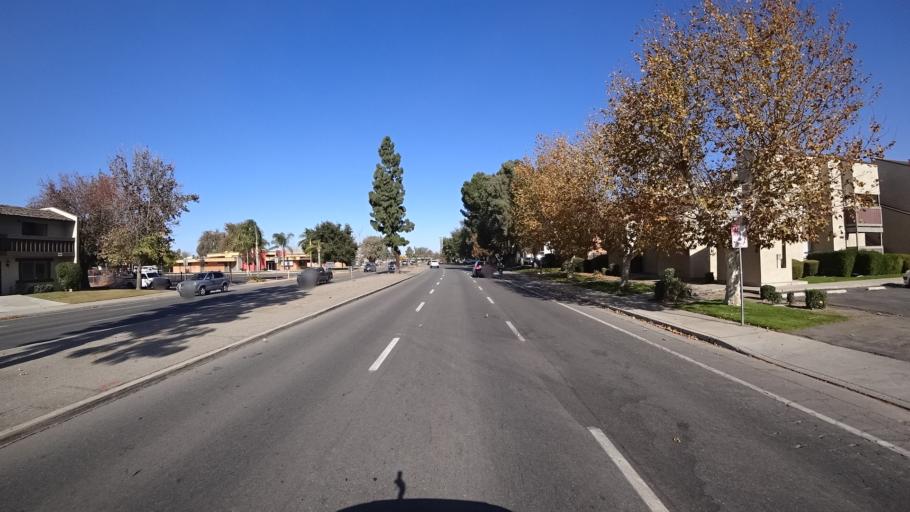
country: US
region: California
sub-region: Kern County
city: Bakersfield
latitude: 35.3275
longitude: -119.0566
